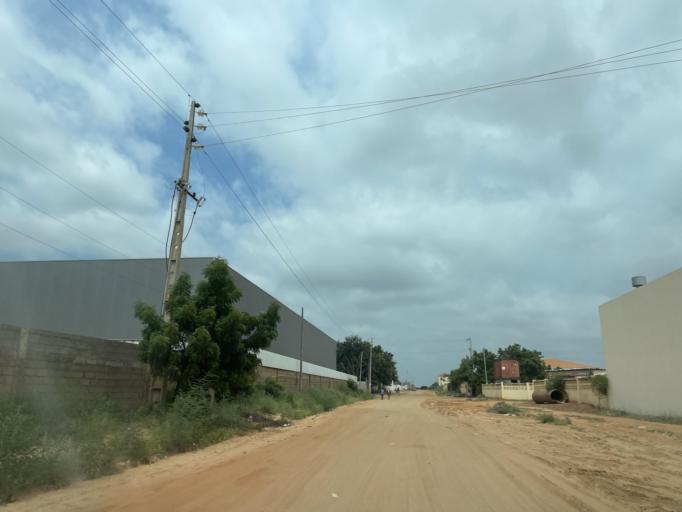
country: AO
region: Luanda
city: Luanda
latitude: -8.9349
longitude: 13.3953
